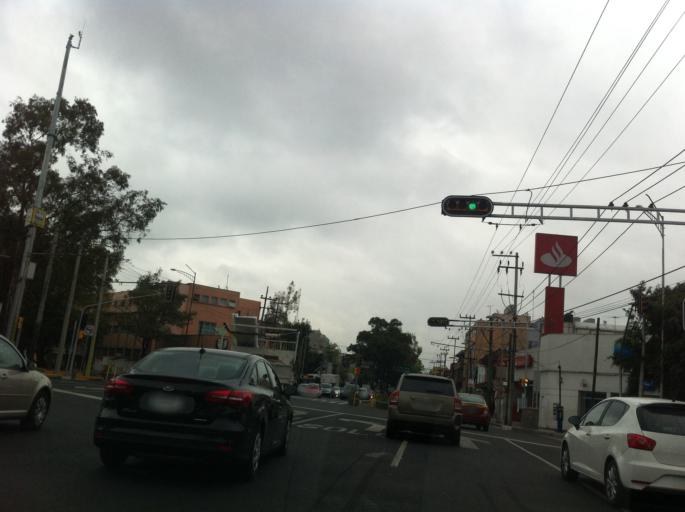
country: MX
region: Mexico City
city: Miguel Hidalgo
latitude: 19.4481
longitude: -99.1823
